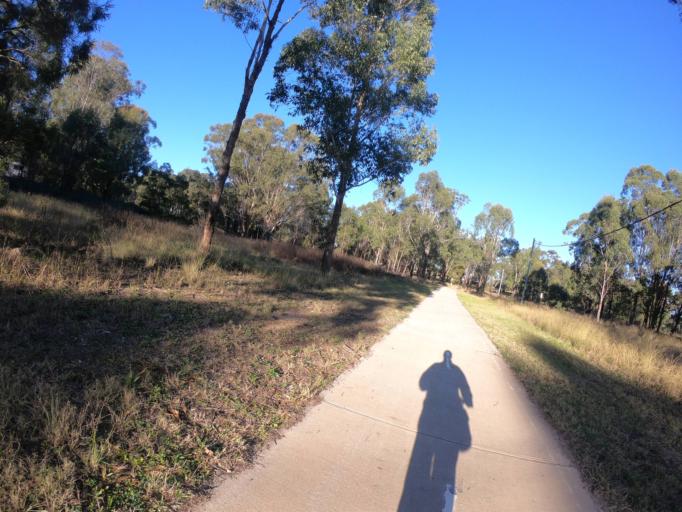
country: AU
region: New South Wales
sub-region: Hawkesbury
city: South Windsor
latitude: -33.6359
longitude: 150.8103
